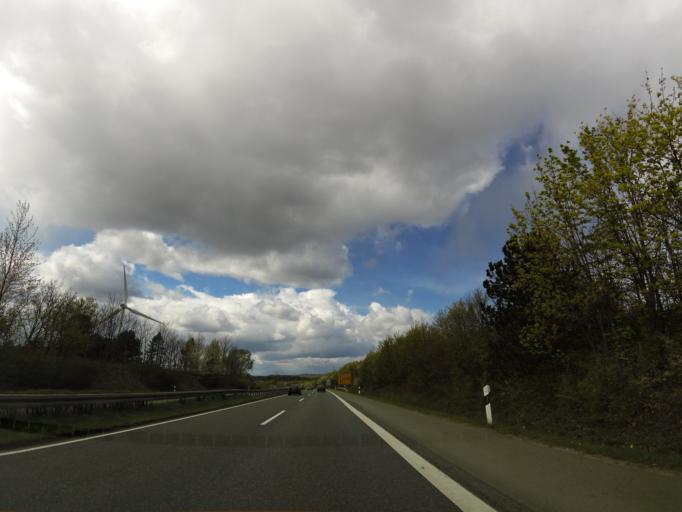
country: DE
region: Lower Saxony
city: Vienenburg
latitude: 51.9216
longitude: 10.5154
